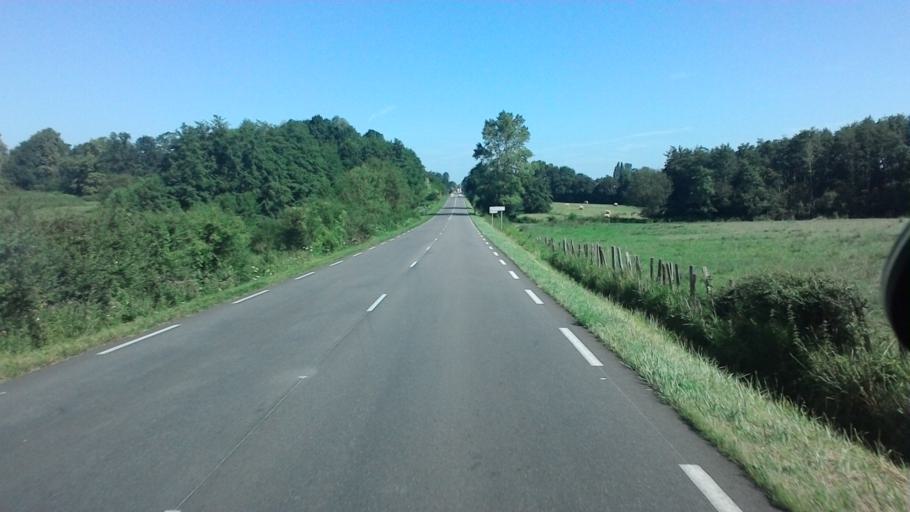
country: FR
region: Bourgogne
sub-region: Departement de Saone-et-Loire
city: Romenay
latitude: 46.4924
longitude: 5.0695
